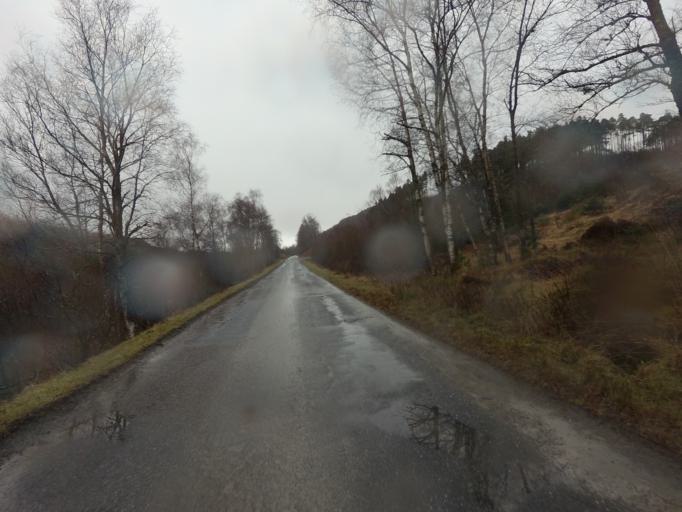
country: GB
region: Scotland
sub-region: West Dunbartonshire
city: Balloch
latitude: 56.2375
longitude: -4.5639
